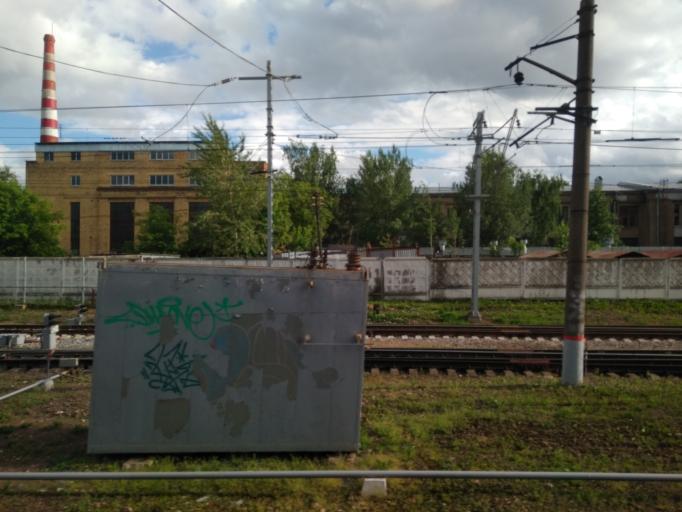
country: RU
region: Moskovskaya
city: Koptevo
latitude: 55.8148
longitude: 37.5074
